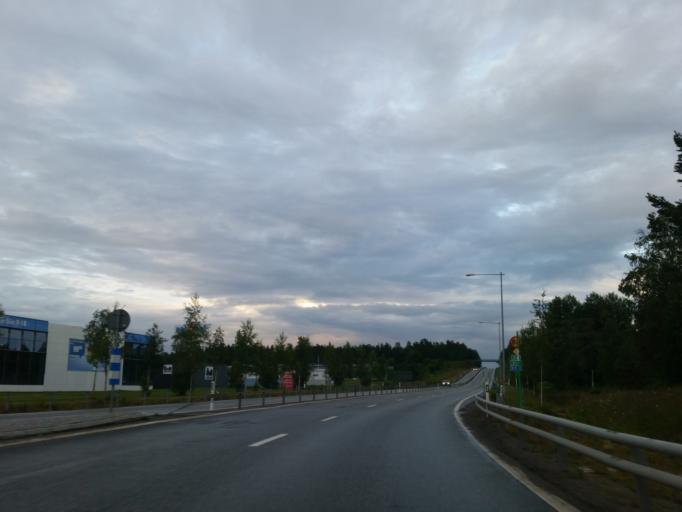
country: SE
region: Vaesterbotten
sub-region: Umea Kommun
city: Ersmark
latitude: 63.8483
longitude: 20.3155
